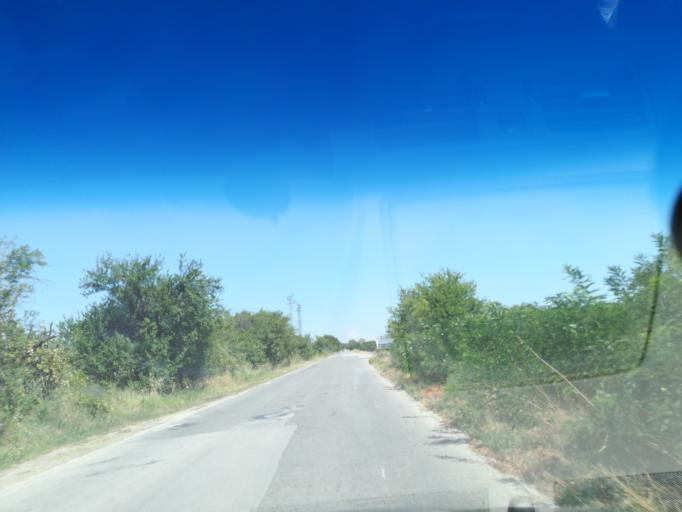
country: BG
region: Plovdiv
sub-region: Obshtina Sadovo
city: Sadovo
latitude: 42.0240
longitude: 24.9994
